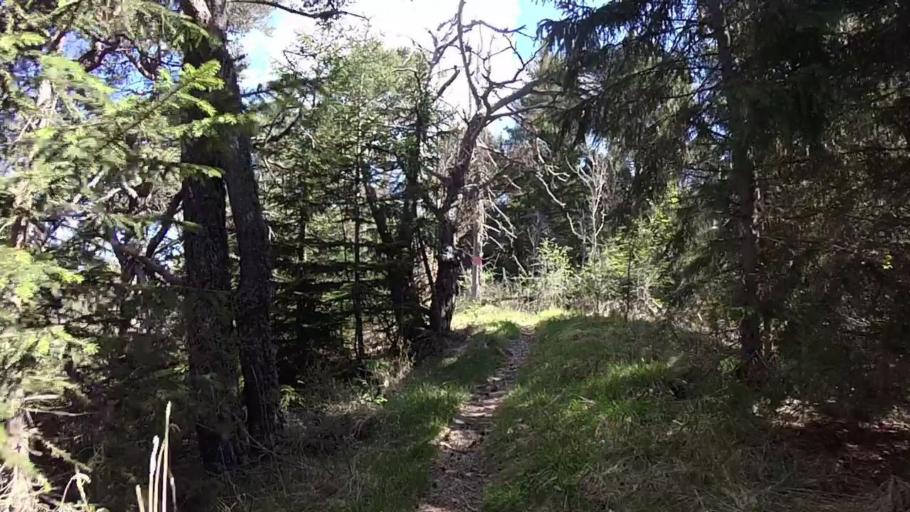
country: FR
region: Provence-Alpes-Cote d'Azur
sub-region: Departement des Alpes-de-Haute-Provence
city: Seyne-les-Alpes
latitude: 44.3213
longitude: 6.3739
